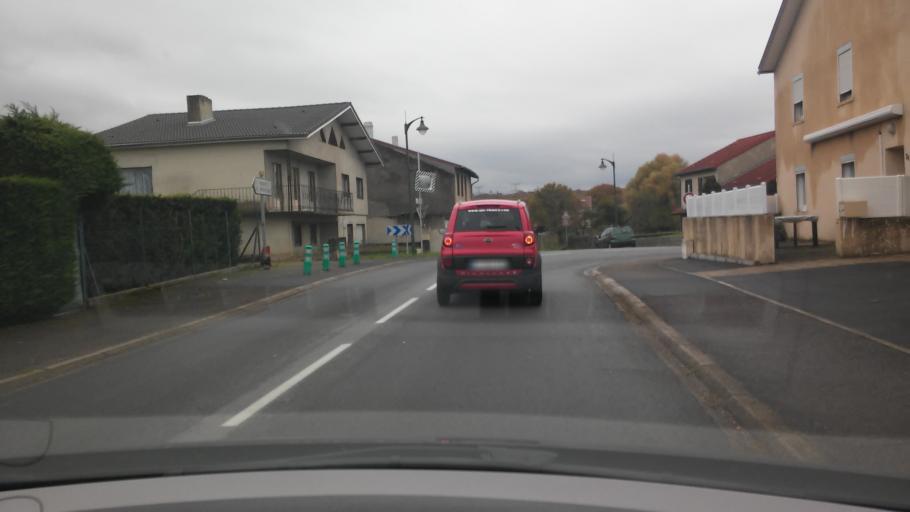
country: FR
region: Lorraine
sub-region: Departement de la Moselle
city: Metzervisse
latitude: 49.2967
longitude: 6.3051
